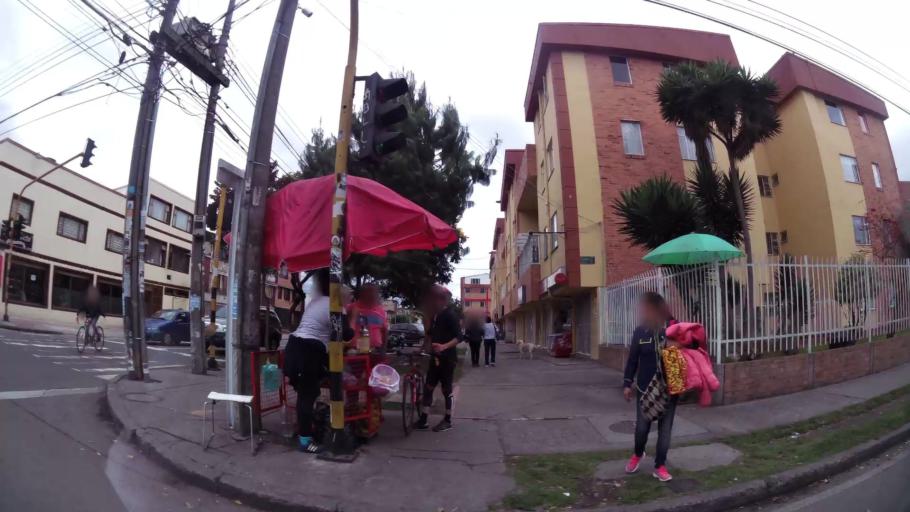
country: CO
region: Bogota D.C.
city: Barrio San Luis
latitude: 4.6893
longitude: -74.0902
